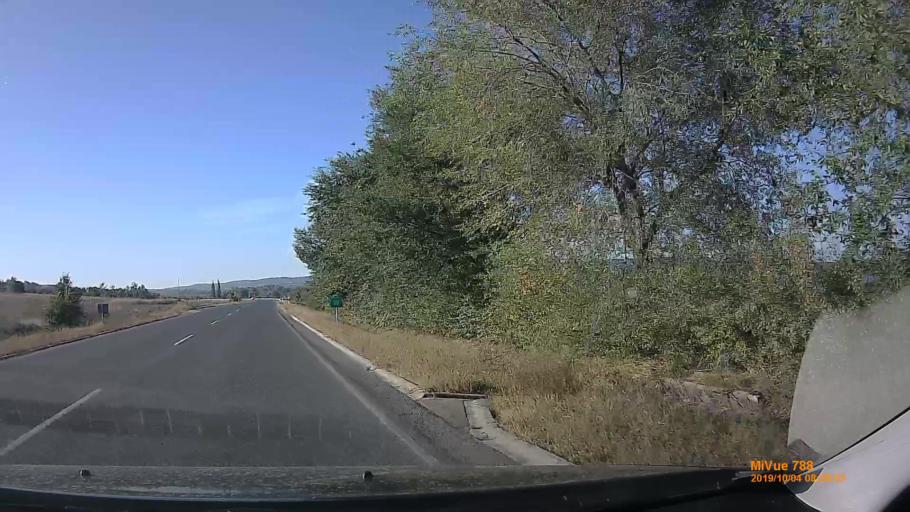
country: HU
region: Somogy
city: Balatonlelle
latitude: 46.7779
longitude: 17.7583
